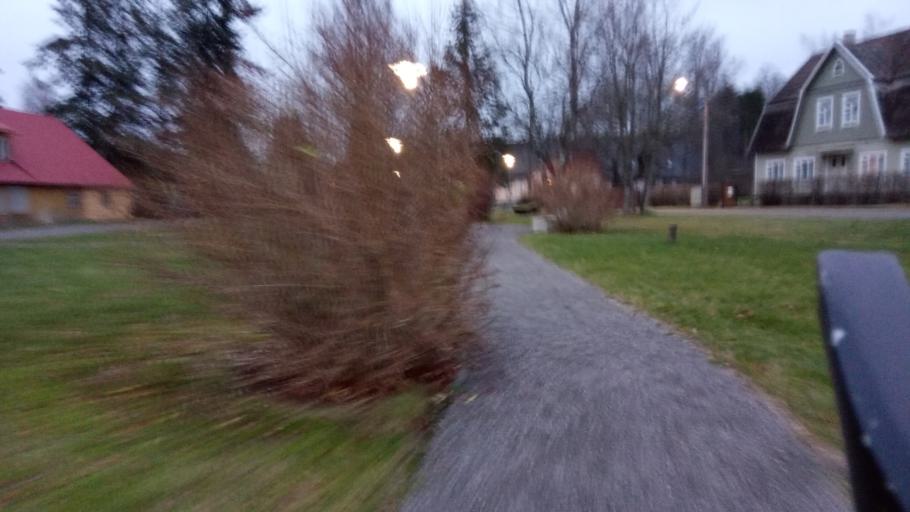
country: EE
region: Harju
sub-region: Kuusalu vald
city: Kuusalu
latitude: 59.4458
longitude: 25.4477
